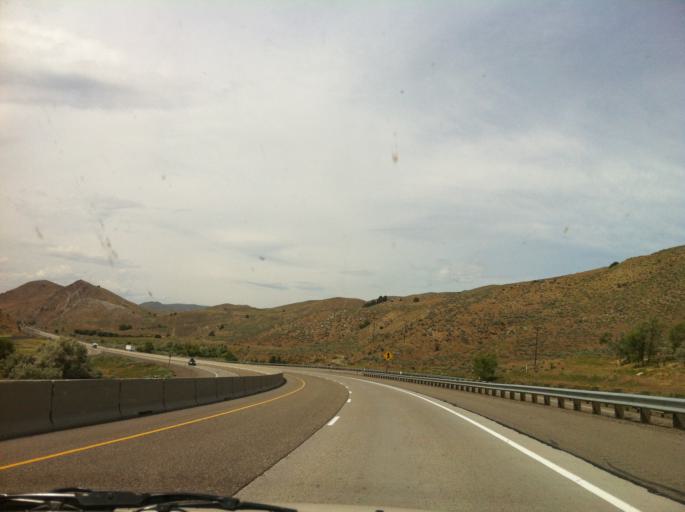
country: US
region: Idaho
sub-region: Washington County
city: Weiser
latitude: 44.3789
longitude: -117.3012
